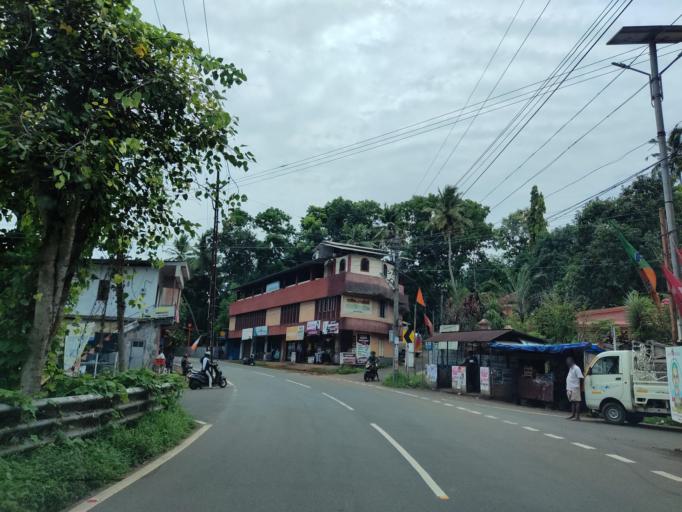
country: IN
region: Kerala
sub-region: Alappuzha
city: Chengannur
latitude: 9.2823
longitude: 76.6147
